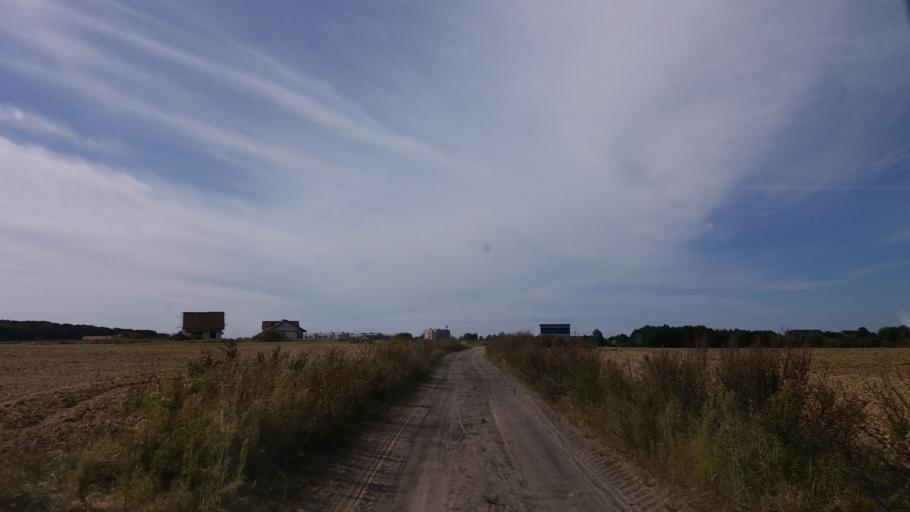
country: PL
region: West Pomeranian Voivodeship
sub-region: Powiat choszczenski
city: Choszczno
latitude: 53.1579
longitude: 15.4457
